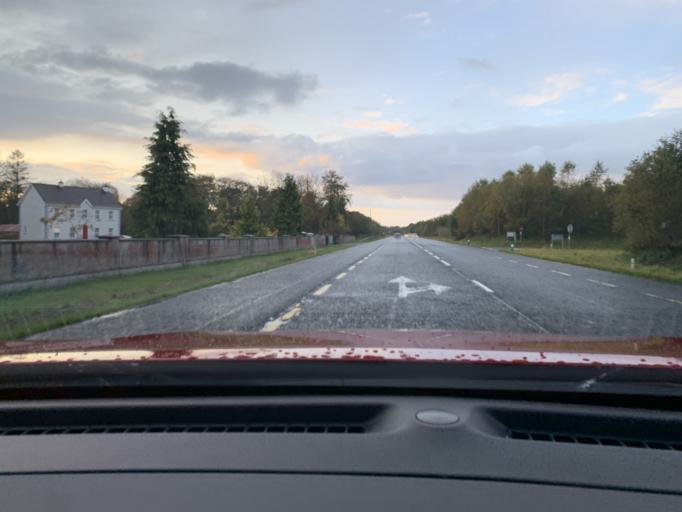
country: IE
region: Connaught
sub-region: County Leitrim
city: Carrick-on-Shannon
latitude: 53.9537
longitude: -8.1555
